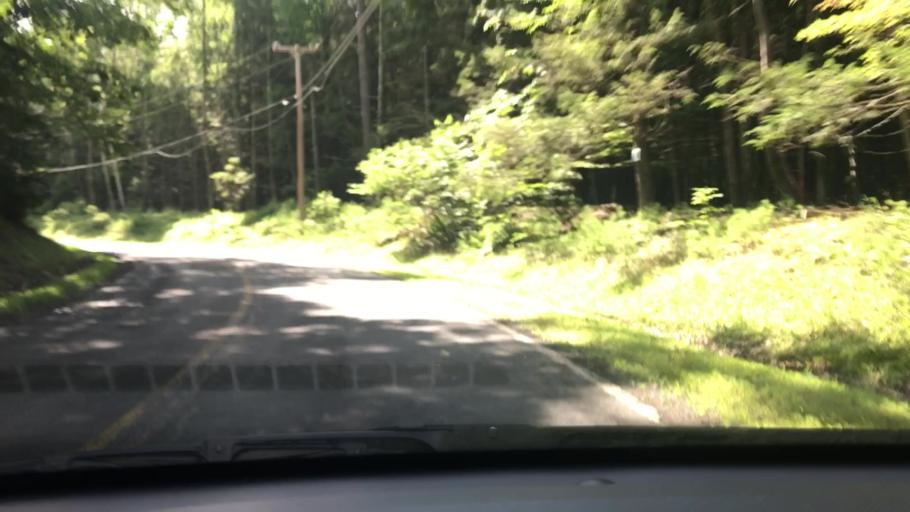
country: US
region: New York
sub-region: Ulster County
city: Shokan
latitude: 41.9518
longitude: -74.2609
